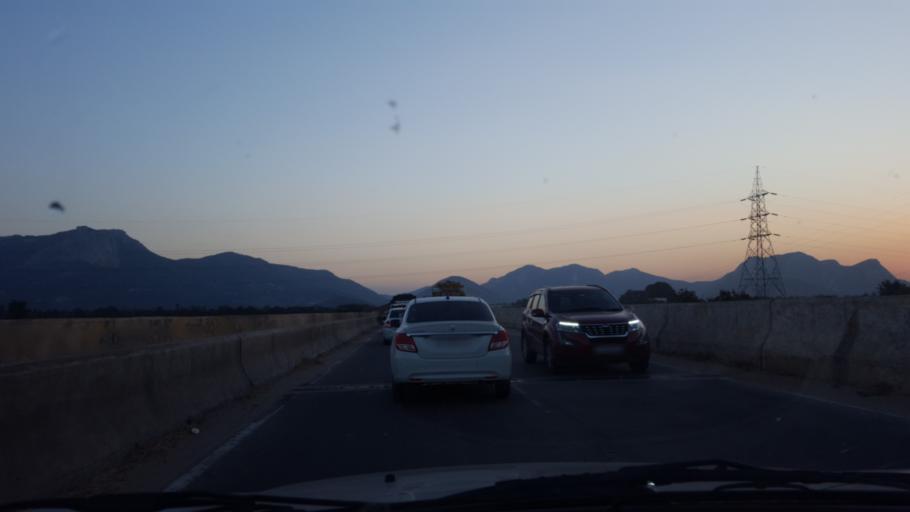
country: IN
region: Andhra Pradesh
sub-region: Chittoor
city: Narasingapuram
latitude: 13.5921
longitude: 79.3455
